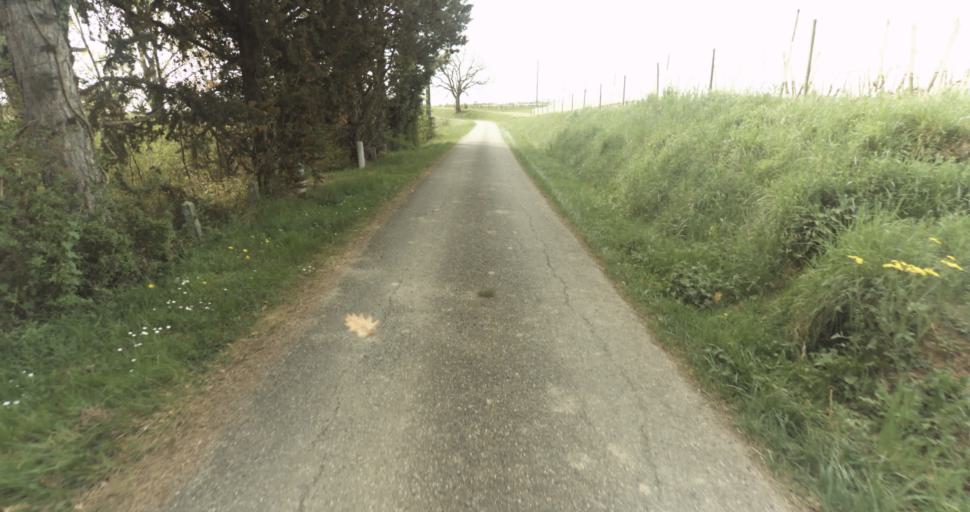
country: FR
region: Midi-Pyrenees
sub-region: Departement du Tarn-et-Garonne
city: Moissac
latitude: 44.1165
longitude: 1.0542
